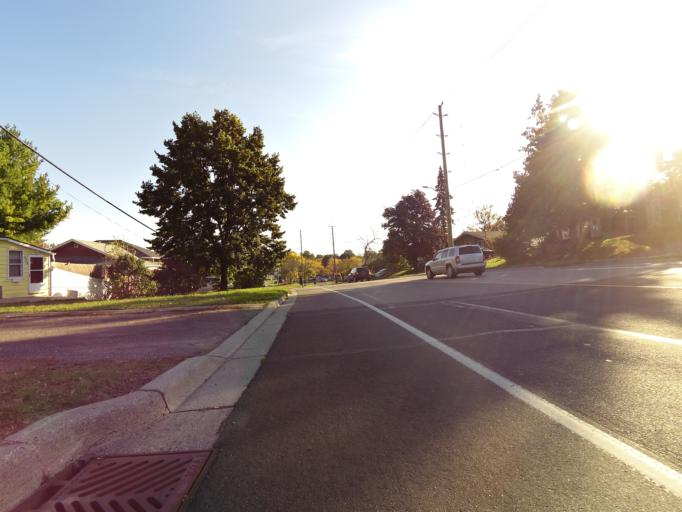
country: CA
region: Ontario
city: Kingston
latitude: 44.2702
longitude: -76.4793
